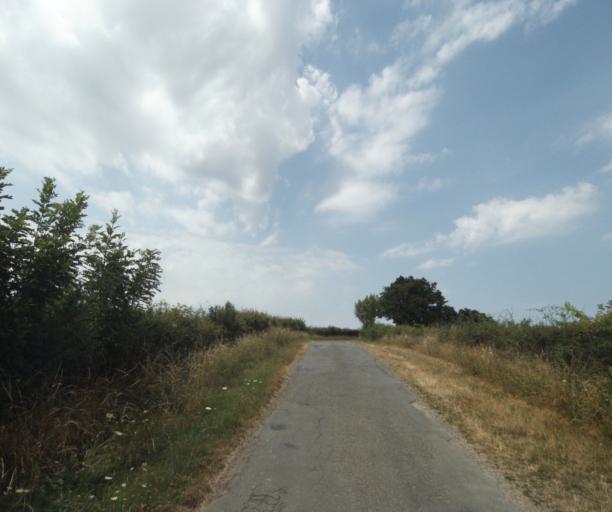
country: FR
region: Bourgogne
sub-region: Departement de Saone-et-Loire
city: Gueugnon
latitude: 46.5838
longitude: 4.0401
